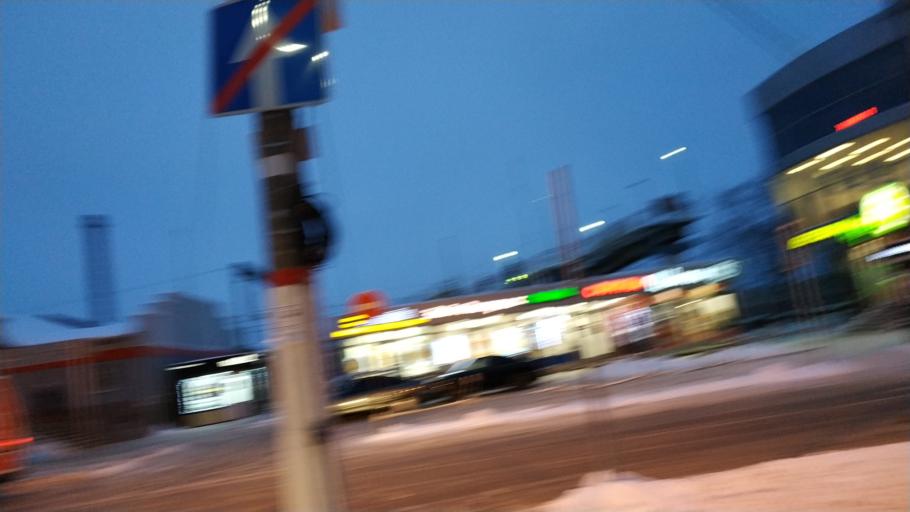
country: RU
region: Moskovskaya
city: Shchelkovo
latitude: 55.9196
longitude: 37.9741
